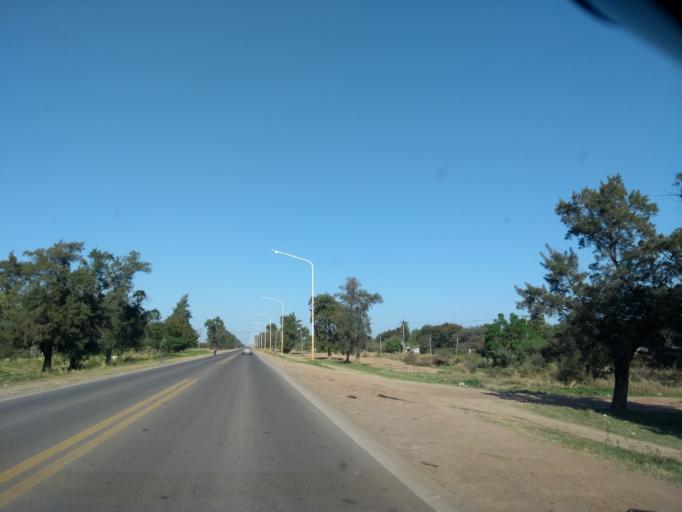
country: AR
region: Chaco
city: Presidencia Roque Saenz Pena
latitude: -26.7873
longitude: -60.4073
